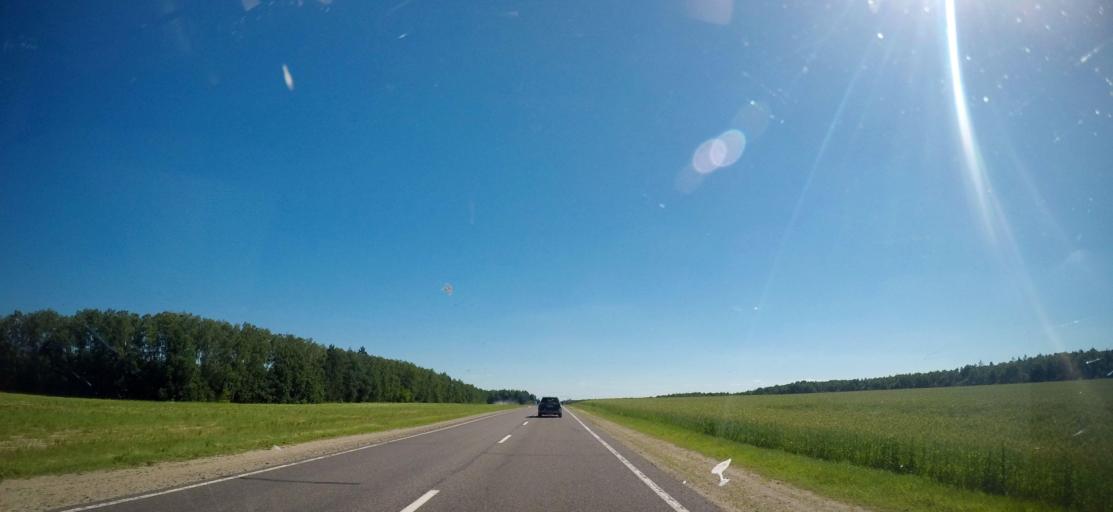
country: BY
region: Grodnenskaya
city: Indura
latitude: 53.5479
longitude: 23.8725
